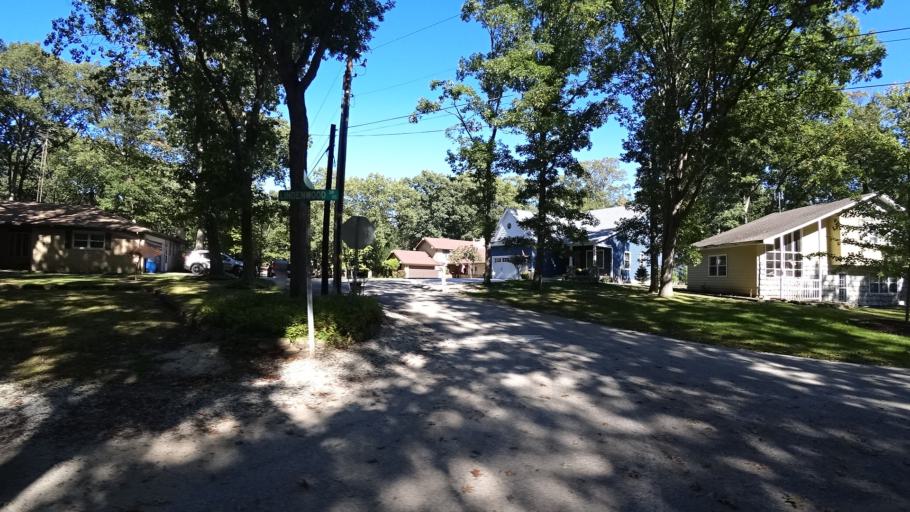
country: US
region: Indiana
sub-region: LaPorte County
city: Long Beach
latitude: 41.7516
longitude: -86.8304
